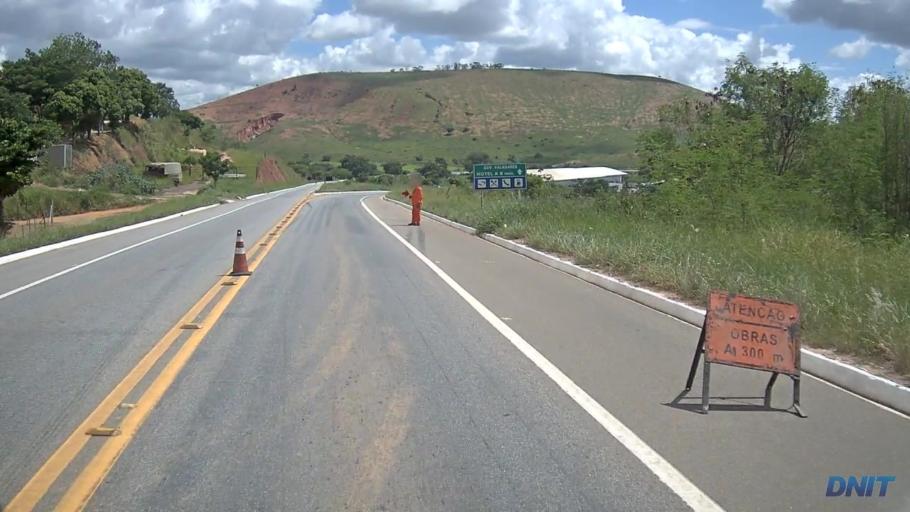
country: BR
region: Minas Gerais
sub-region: Governador Valadares
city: Governador Valadares
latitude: -18.8937
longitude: -42.0047
